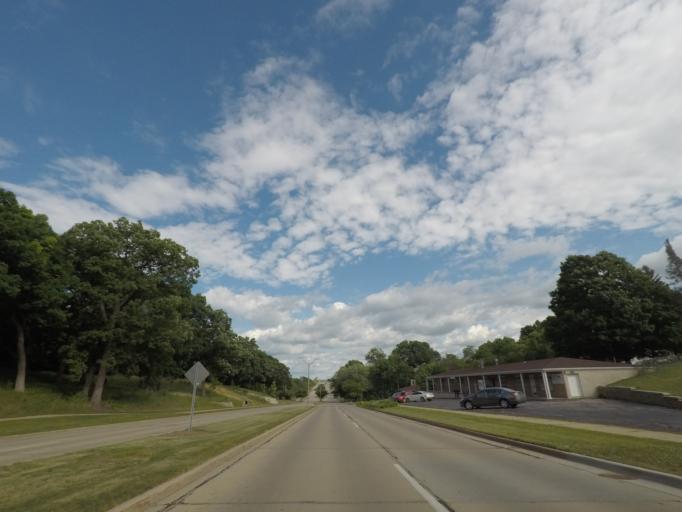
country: US
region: Wisconsin
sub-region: Rock County
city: Janesville
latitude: 42.6780
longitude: -88.9978
